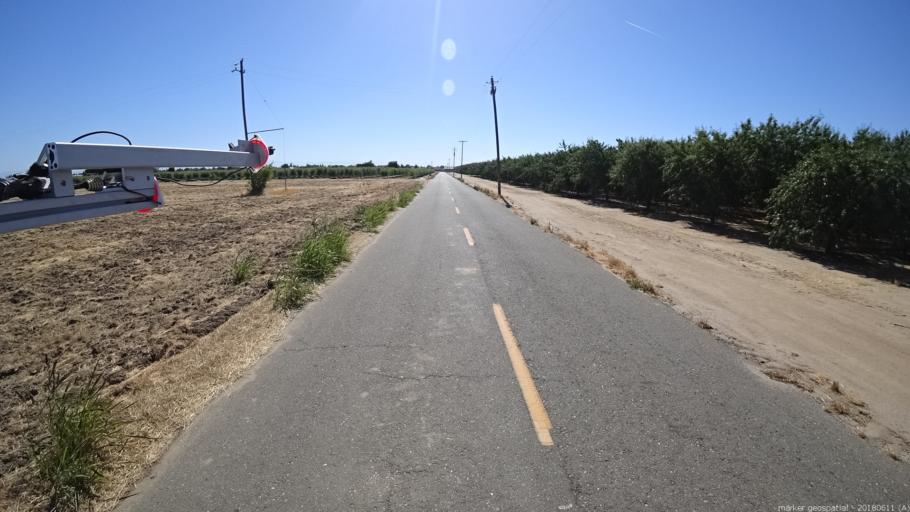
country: US
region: California
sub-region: Madera County
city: Madera
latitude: 36.9492
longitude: -120.1055
